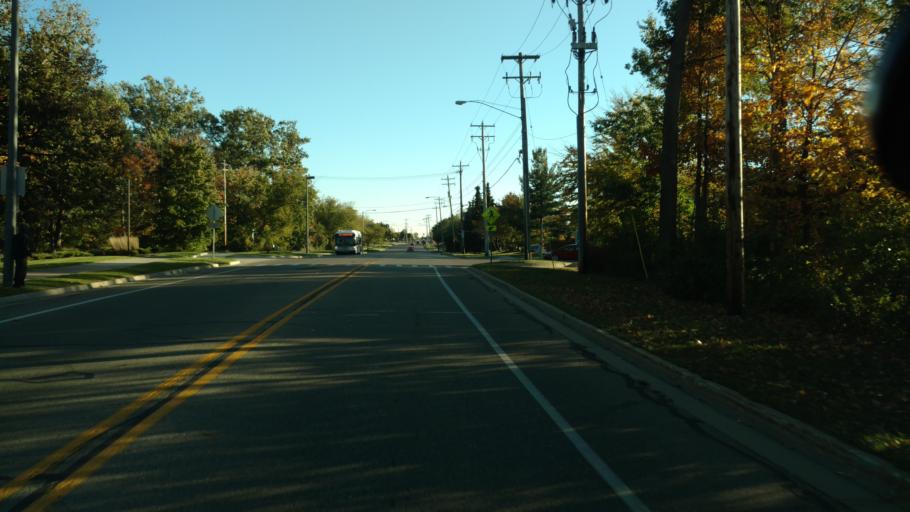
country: US
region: Michigan
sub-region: Ingham County
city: East Lansing
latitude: 42.7654
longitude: -84.5033
